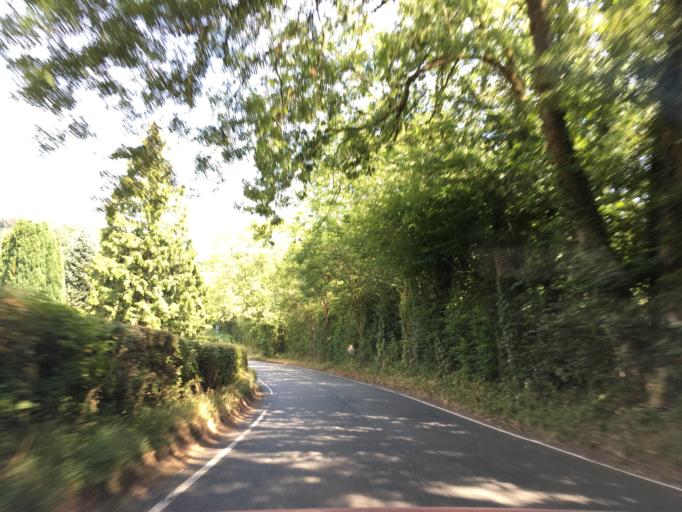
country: GB
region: Wales
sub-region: Newport
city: Langstone
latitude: 51.6123
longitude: -2.9147
